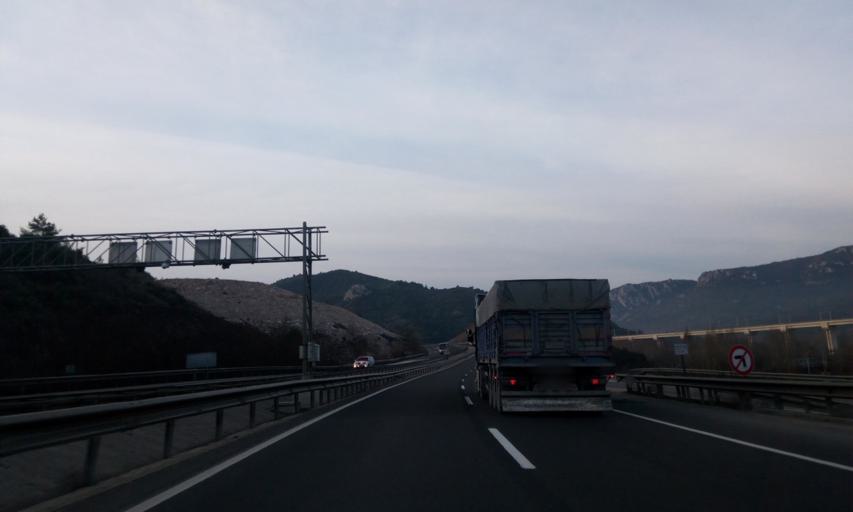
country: TR
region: Bilecik
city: Bilecik
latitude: 40.1616
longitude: 30.0207
